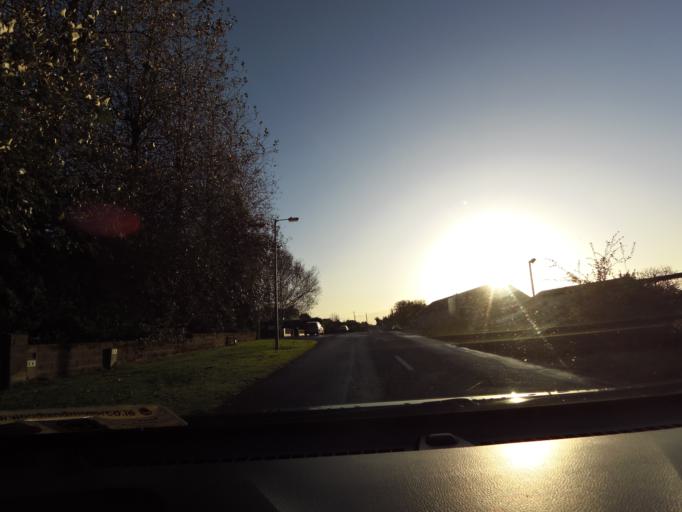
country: IE
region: Connaught
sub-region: Roscommon
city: Castlerea
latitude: 53.7577
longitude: -8.5168
